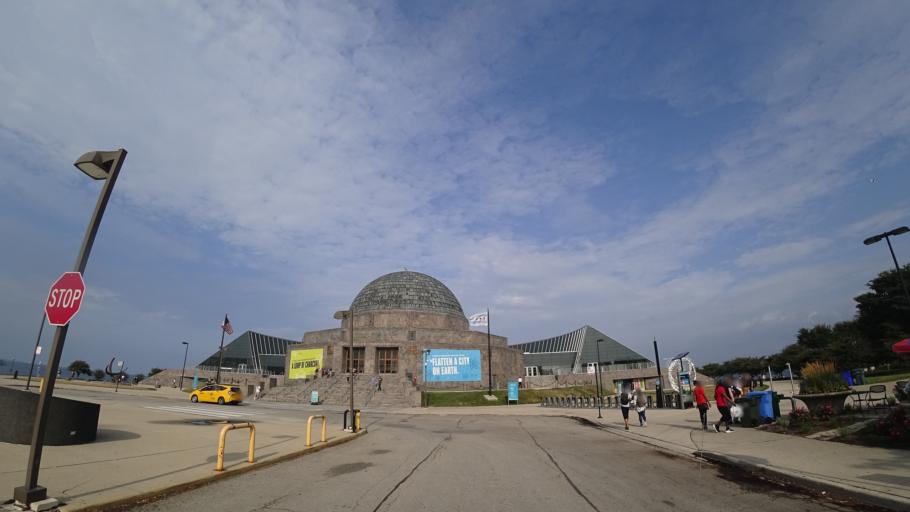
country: US
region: Illinois
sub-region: Cook County
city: Chicago
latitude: 41.8662
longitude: -87.6077
